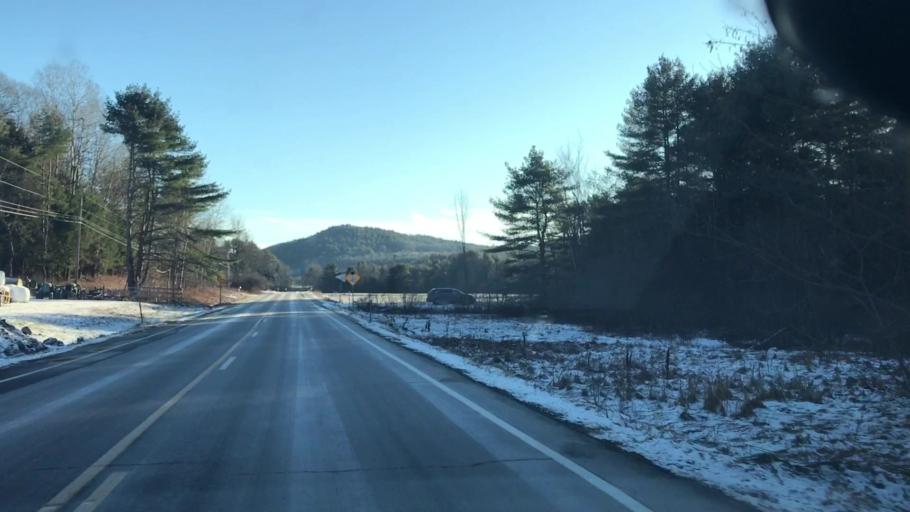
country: US
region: New Hampshire
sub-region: Grafton County
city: Lyme Town Offices
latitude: 43.8543
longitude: -72.1558
